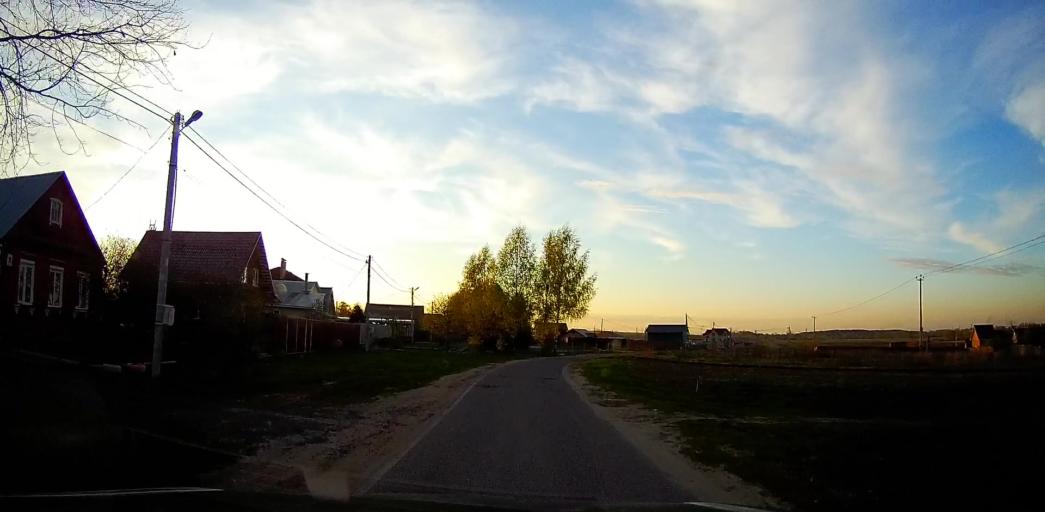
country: RU
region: Moskovskaya
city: Peski
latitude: 55.2116
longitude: 38.7400
